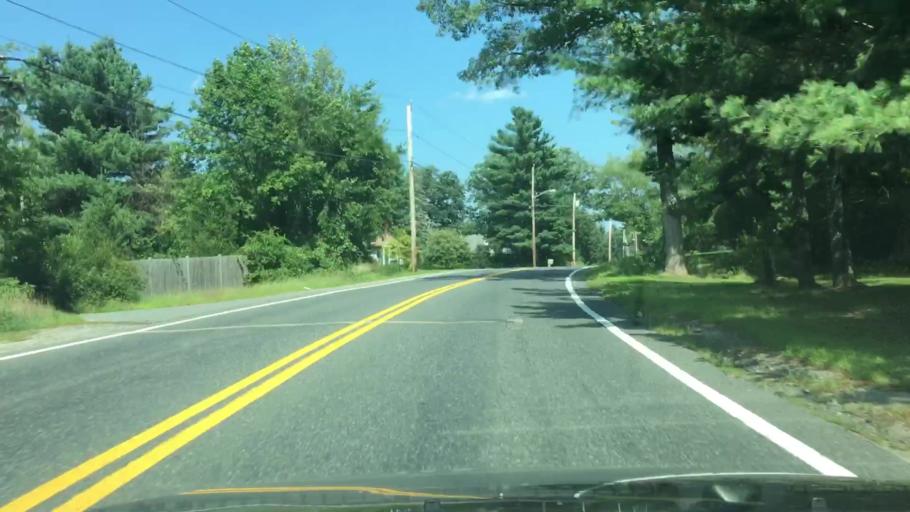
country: US
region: Massachusetts
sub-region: Worcester County
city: Milford
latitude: 42.1687
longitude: -71.4776
